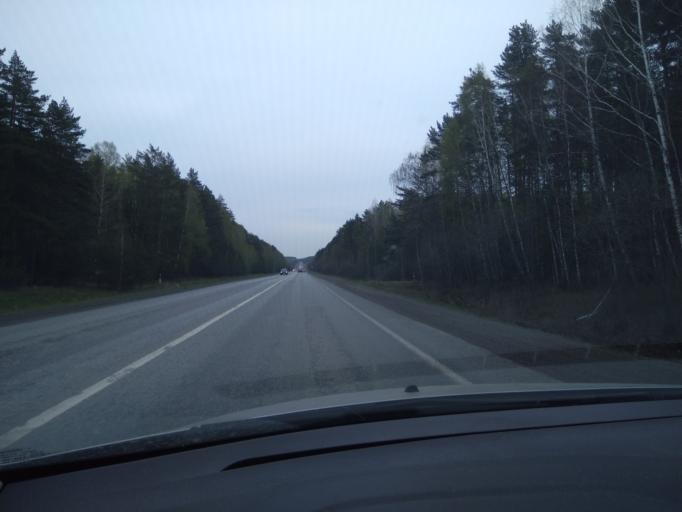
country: RU
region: Sverdlovsk
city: Gryaznovskoye
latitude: 56.7884
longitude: 61.7350
